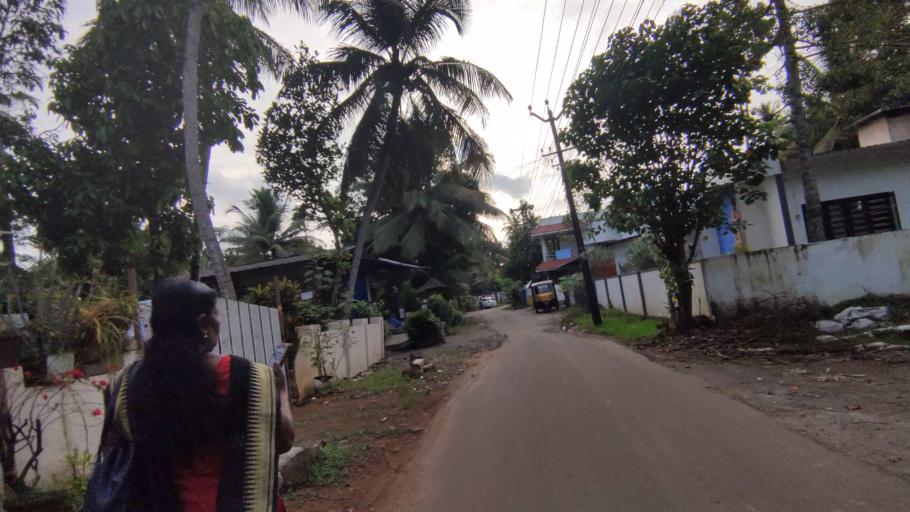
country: IN
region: Kerala
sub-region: Kottayam
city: Kottayam
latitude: 9.6037
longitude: 76.4384
